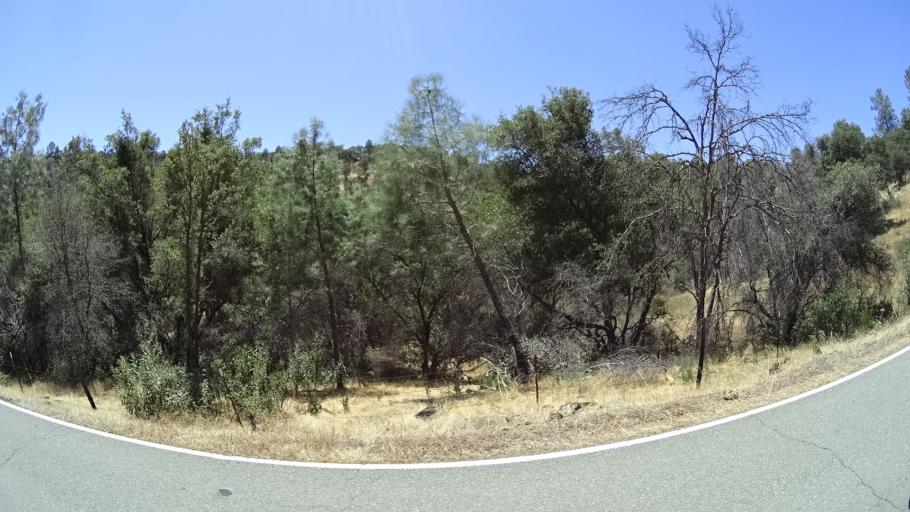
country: US
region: California
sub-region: Calaveras County
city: San Andreas
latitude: 38.2974
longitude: -120.6806
